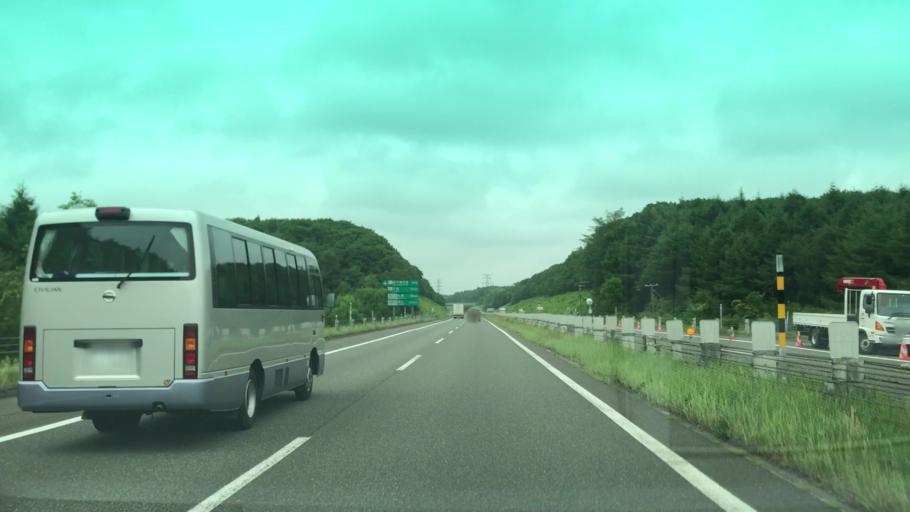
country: JP
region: Hokkaido
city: Chitose
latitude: 42.7228
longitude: 141.6528
